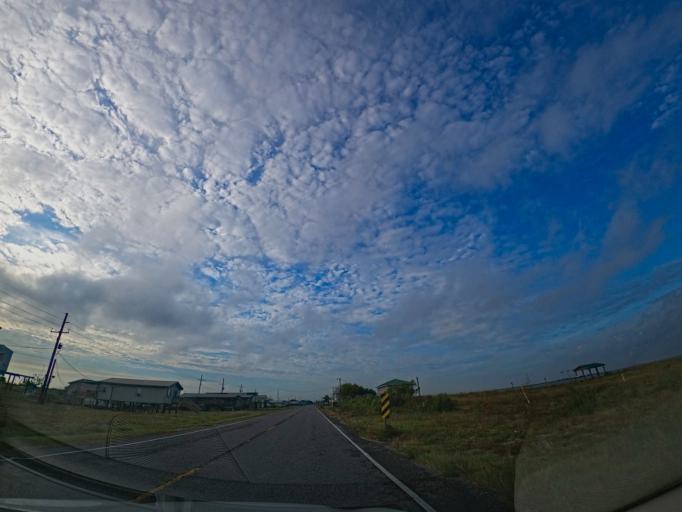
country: US
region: Louisiana
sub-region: Terrebonne Parish
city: Chauvin
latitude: 29.3577
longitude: -90.6261
